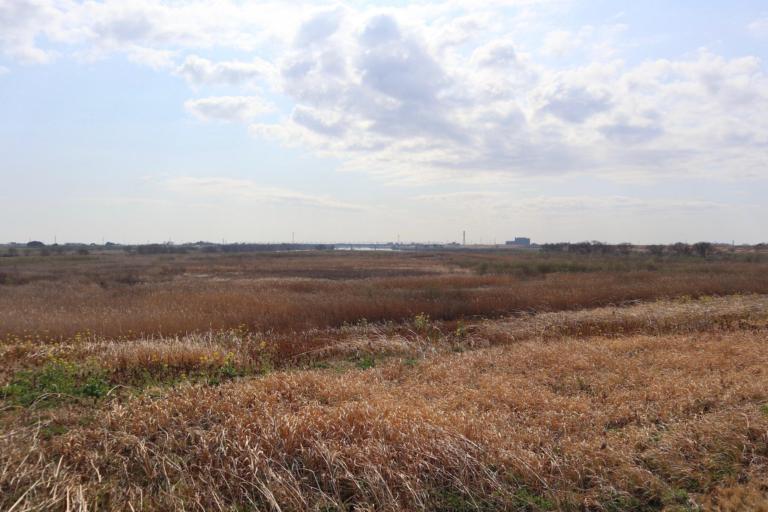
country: JP
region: Ibaraki
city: Koga
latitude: 36.1643
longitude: 139.6909
